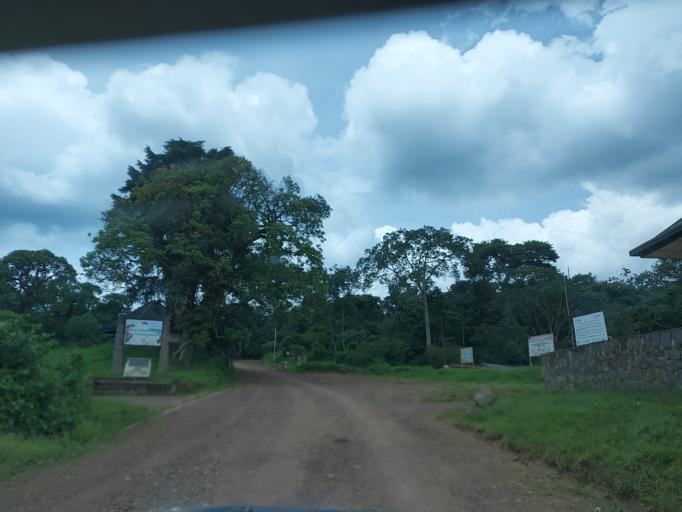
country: CD
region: South Kivu
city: Kabare
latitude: -2.3149
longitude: 28.7586
